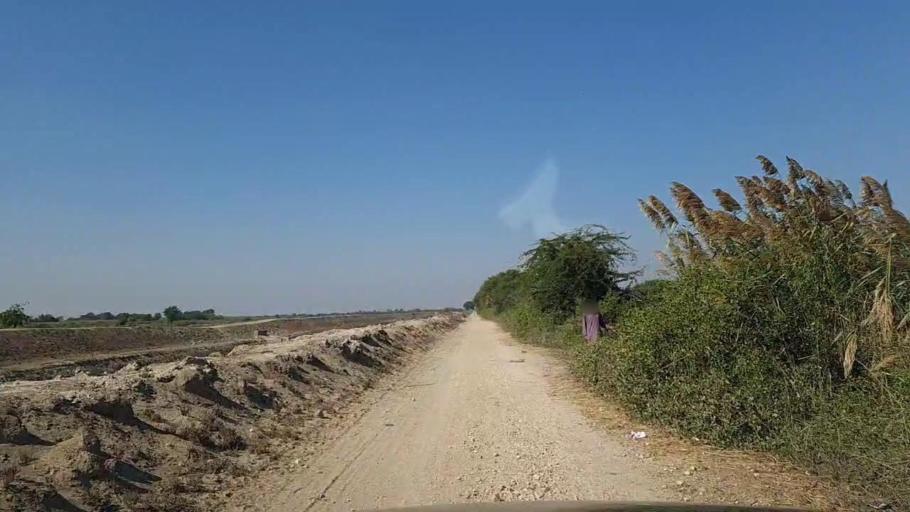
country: PK
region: Sindh
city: Mirpur Batoro
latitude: 24.7180
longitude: 68.2361
